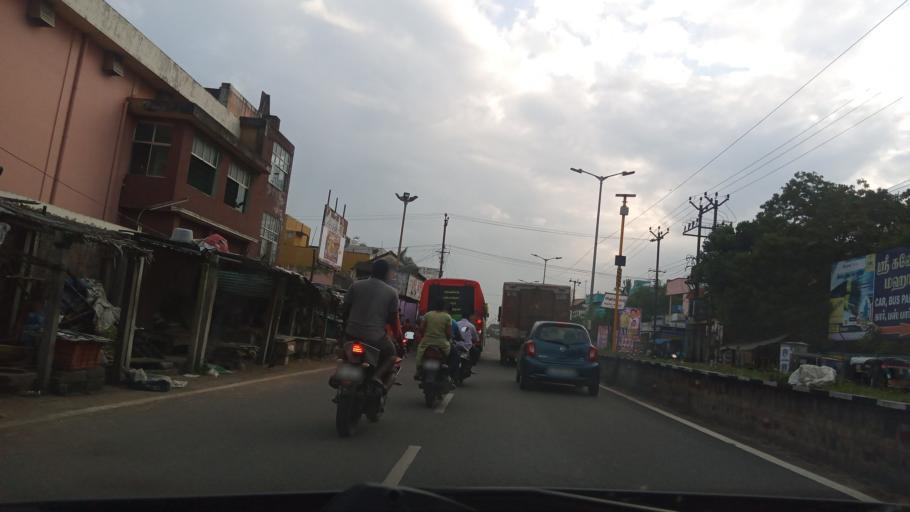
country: IN
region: Tamil Nadu
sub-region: Villupuram
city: Auroville
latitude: 12.0299
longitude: 79.8636
